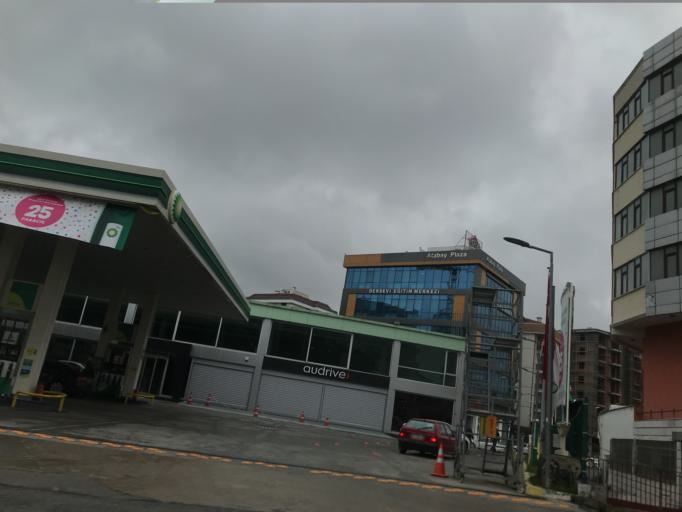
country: TR
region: Istanbul
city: Pendik
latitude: 40.8851
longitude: 29.2360
